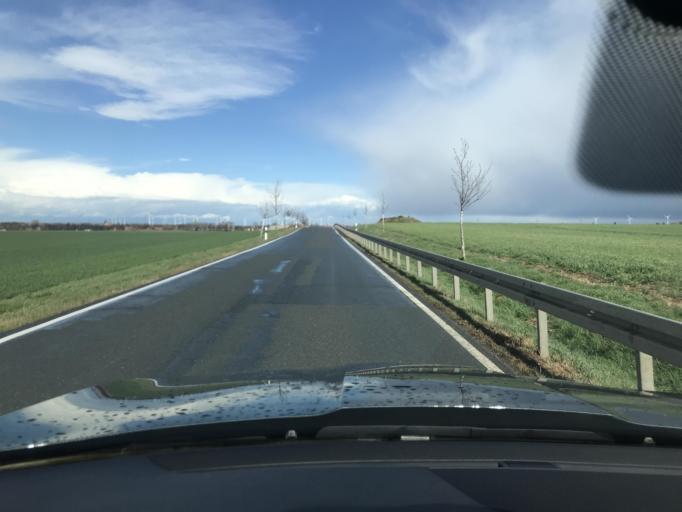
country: DE
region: Saxony-Anhalt
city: Hoym
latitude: 51.7219
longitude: 11.3217
